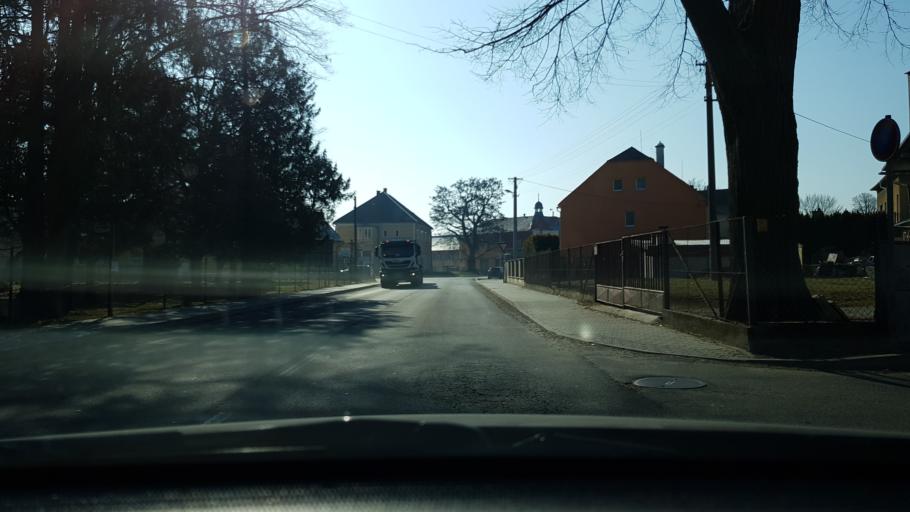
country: CZ
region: Olomoucky
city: Postrelmov
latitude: 49.9100
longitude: 16.9130
